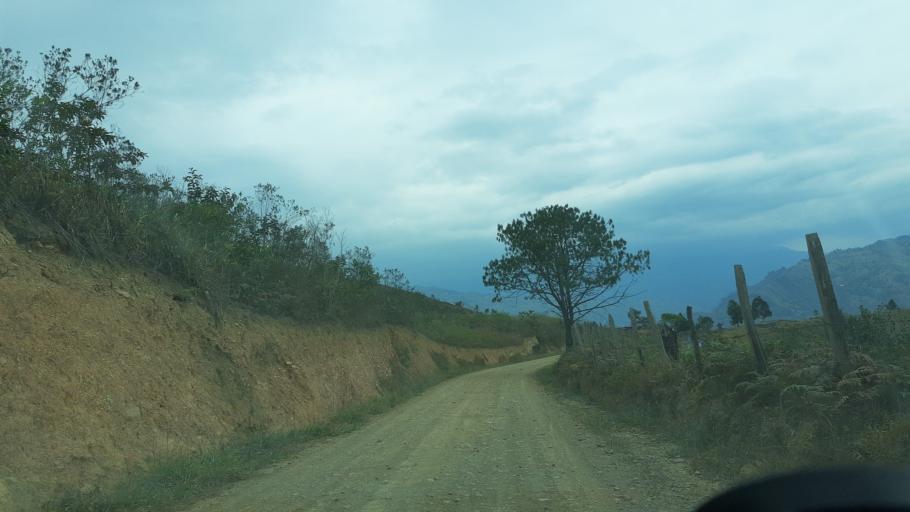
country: CO
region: Boyaca
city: Somondoco
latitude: 4.9869
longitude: -73.3747
